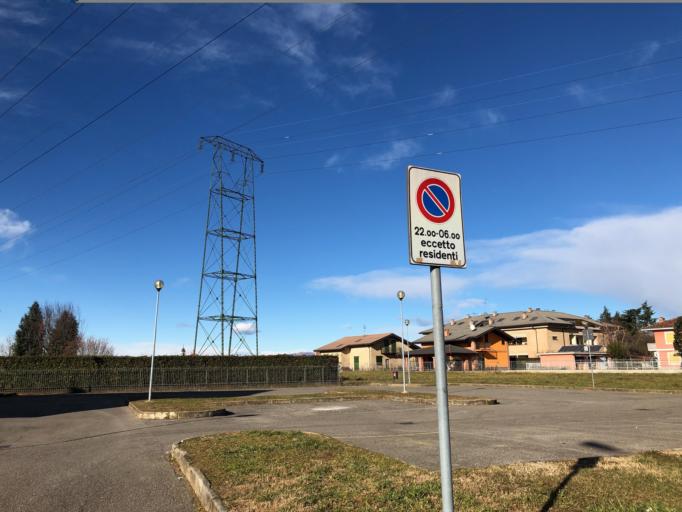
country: IT
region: Lombardy
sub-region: Provincia di Monza e Brianza
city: Sulbiate
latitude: 45.6368
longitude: 9.4216
